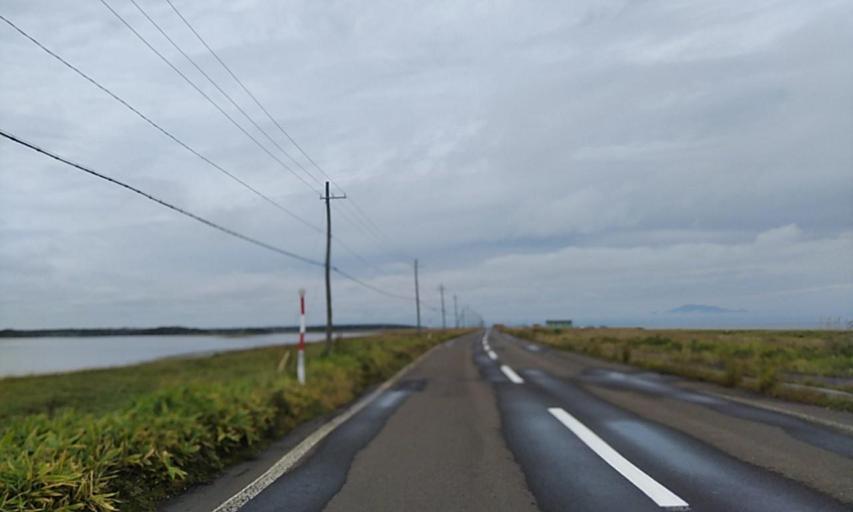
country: JP
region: Hokkaido
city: Shibetsu
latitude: 43.5988
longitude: 145.3152
